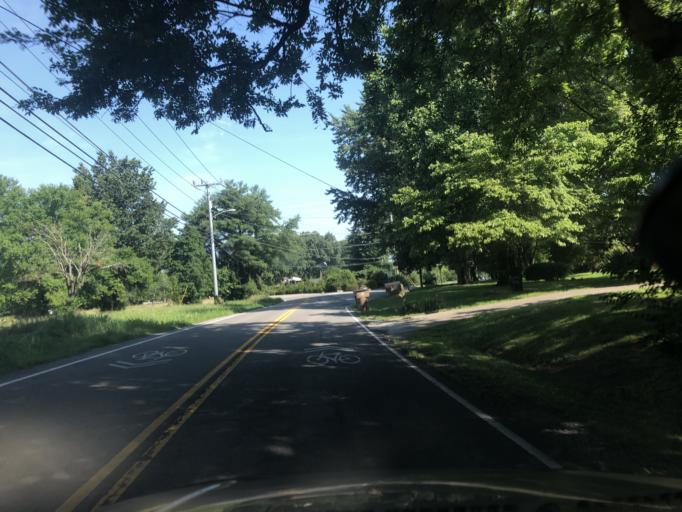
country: US
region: Tennessee
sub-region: Davidson County
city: Lakewood
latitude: 36.2332
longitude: -86.6991
